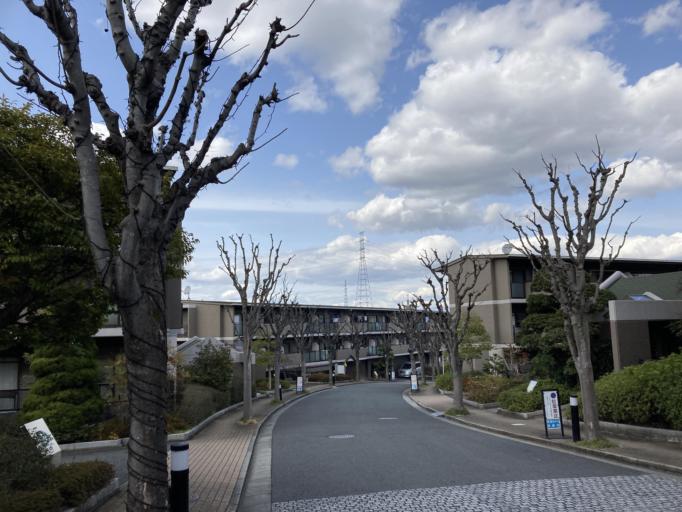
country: JP
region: Nara
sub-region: Ikoma-shi
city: Ikoma
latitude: 34.7076
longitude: 135.6993
